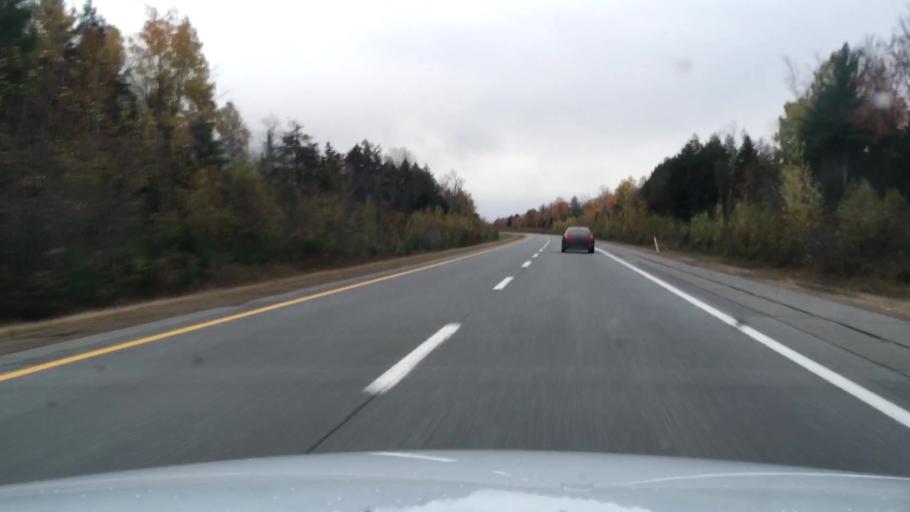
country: US
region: Maine
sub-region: Penobscot County
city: Greenbush
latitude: 45.0999
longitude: -68.6962
